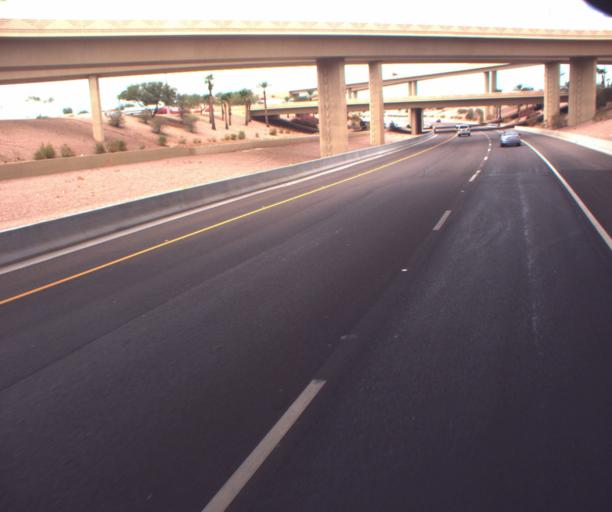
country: US
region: Arizona
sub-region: Maricopa County
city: Guadalupe
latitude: 33.2970
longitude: -111.9701
